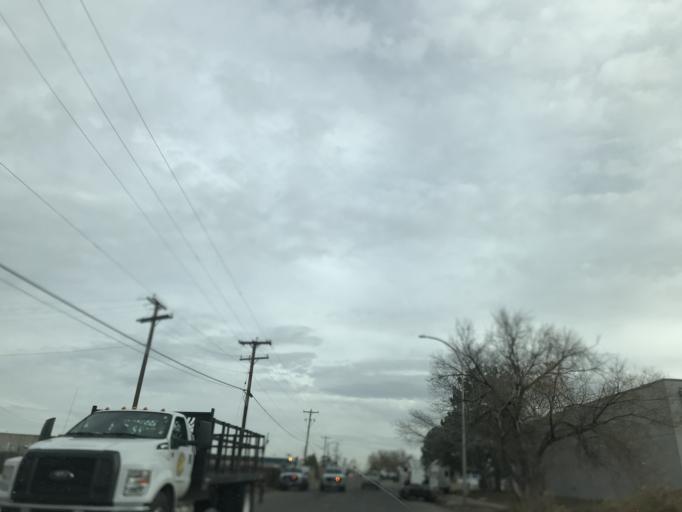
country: US
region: Colorado
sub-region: Adams County
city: Commerce City
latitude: 39.7838
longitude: -104.9132
